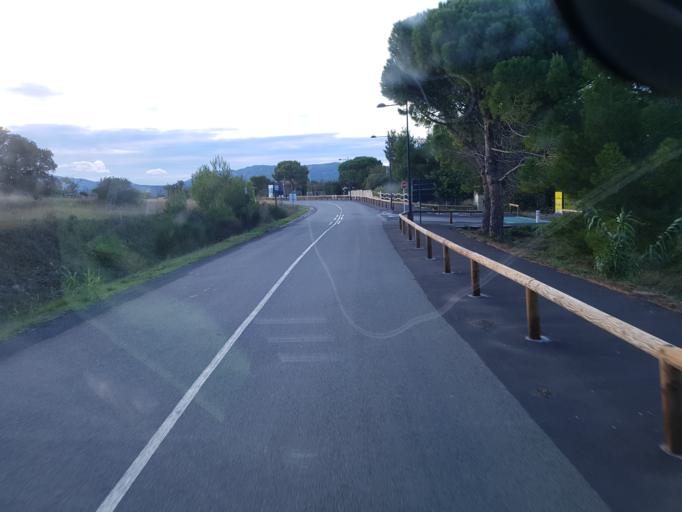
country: FR
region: Languedoc-Roussillon
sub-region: Departement de l'Aude
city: Leucate
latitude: 42.9340
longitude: 3.0175
